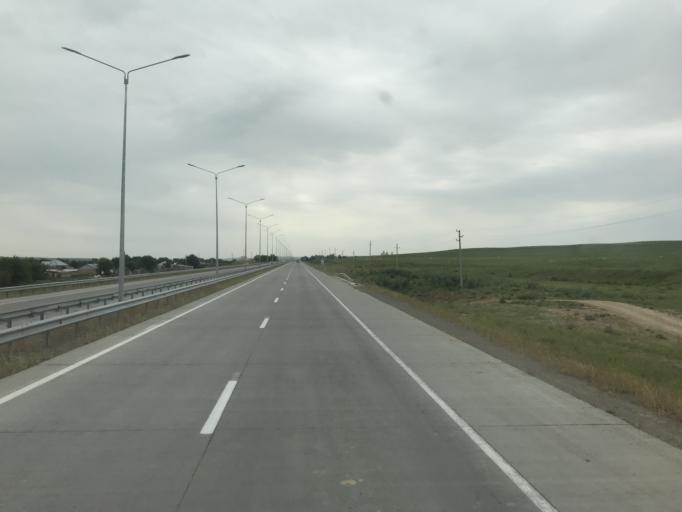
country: KZ
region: Ongtustik Qazaqstan
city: Qazyqurt
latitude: 41.8905
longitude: 69.4471
